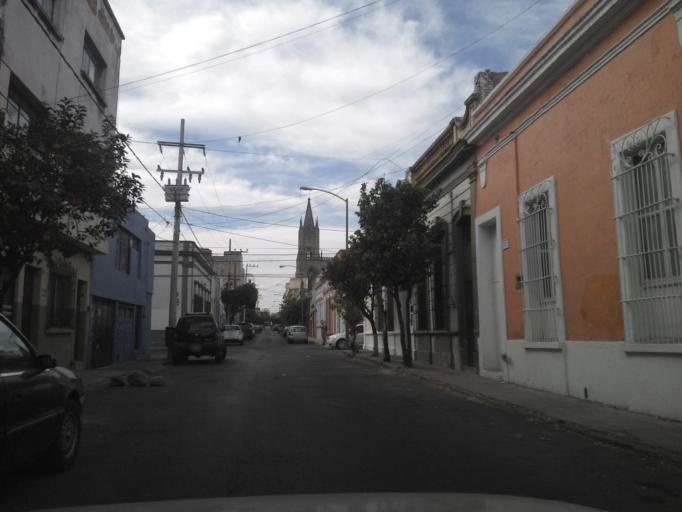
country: MX
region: Jalisco
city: Guadalajara
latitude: 20.6734
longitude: -103.3565
